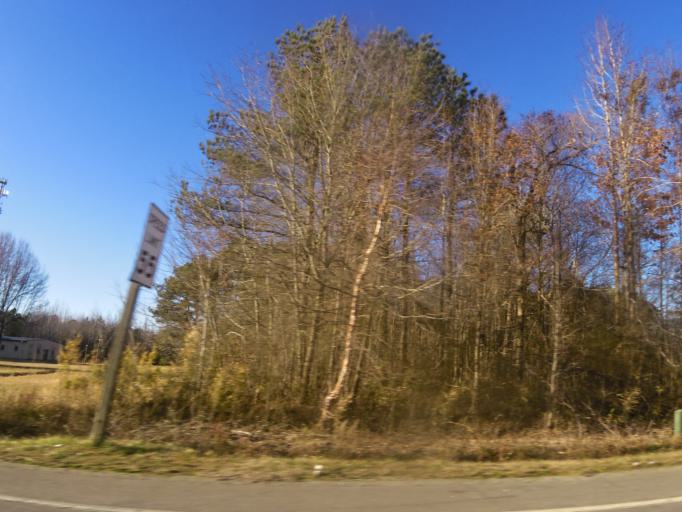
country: US
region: Virginia
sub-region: Isle of Wight County
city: Windsor
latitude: 36.6972
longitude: -76.7118
